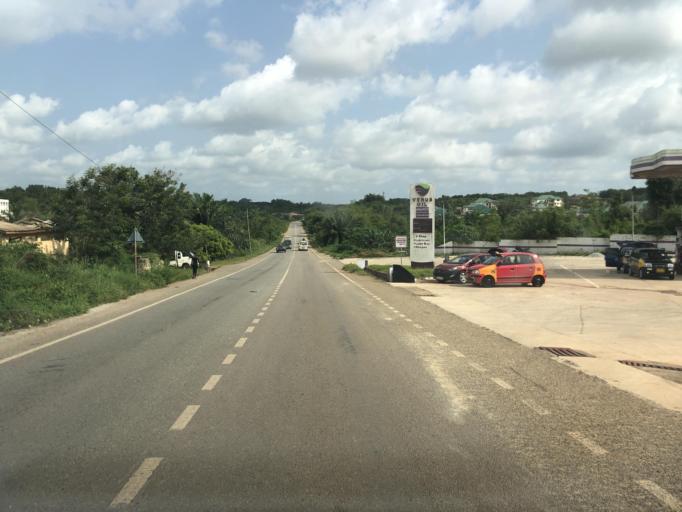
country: GH
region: Central
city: Elmina
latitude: 5.1937
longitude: -1.3186
